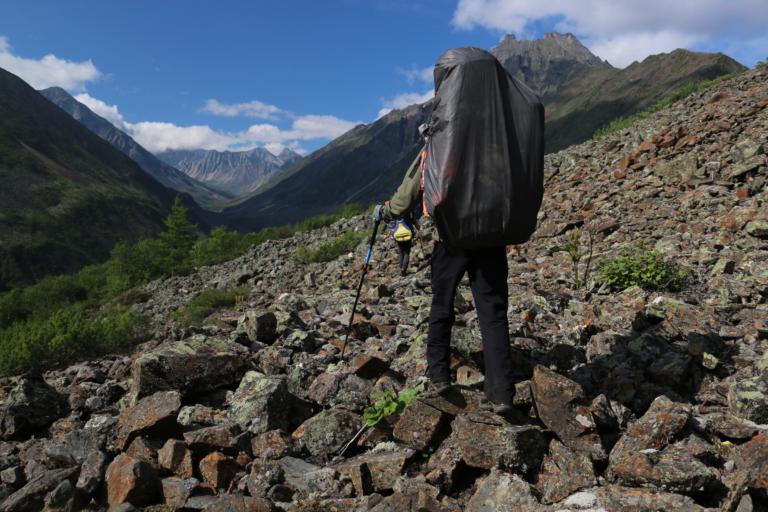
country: RU
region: Respublika Buryatiya
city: Novyy Uoyan
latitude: 56.2985
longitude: 111.3337
